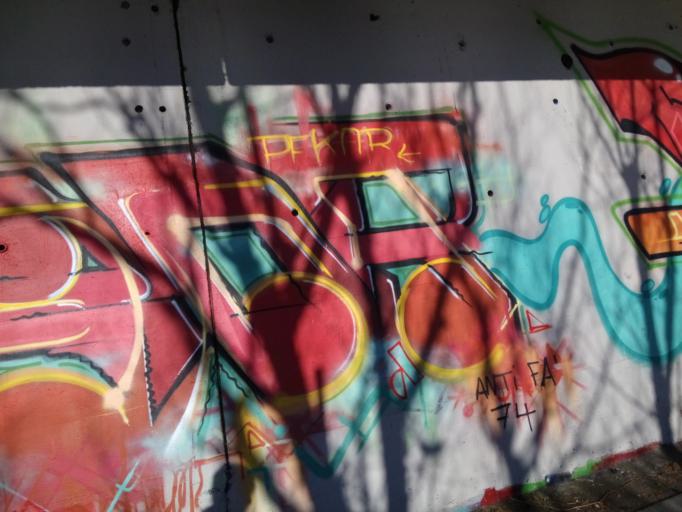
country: FR
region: Rhone-Alpes
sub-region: Departement de l'Isere
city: Saint-Martin-le-Vinoux
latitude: 45.2037
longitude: 5.7127
